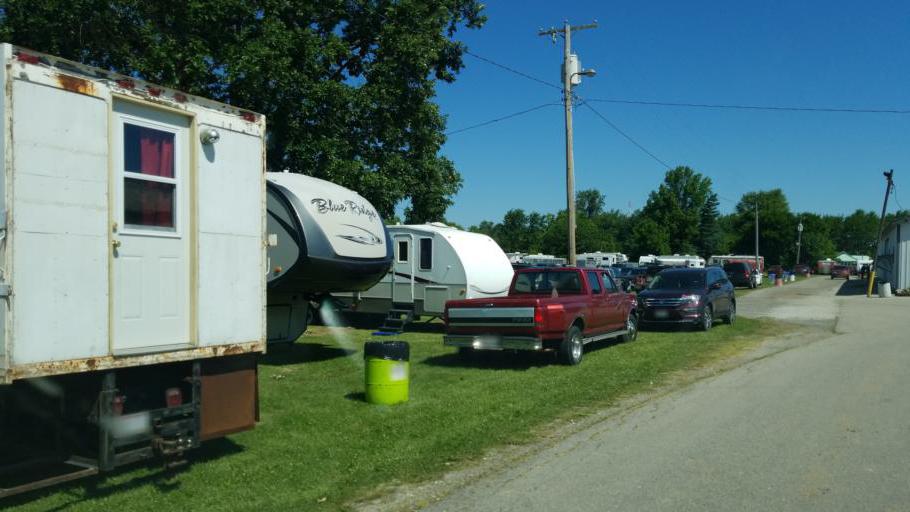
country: US
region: Ohio
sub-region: Marion County
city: Marion
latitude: 40.6035
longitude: -83.1264
